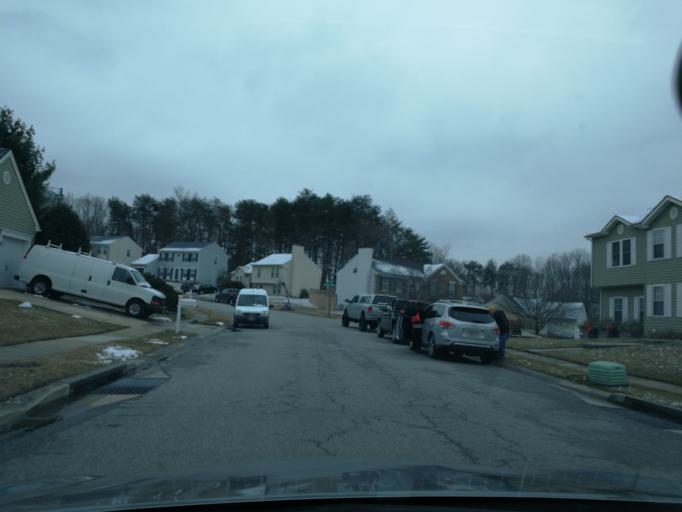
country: US
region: Maryland
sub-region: Harford County
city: Bel Air South
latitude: 39.4693
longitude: -76.2971
